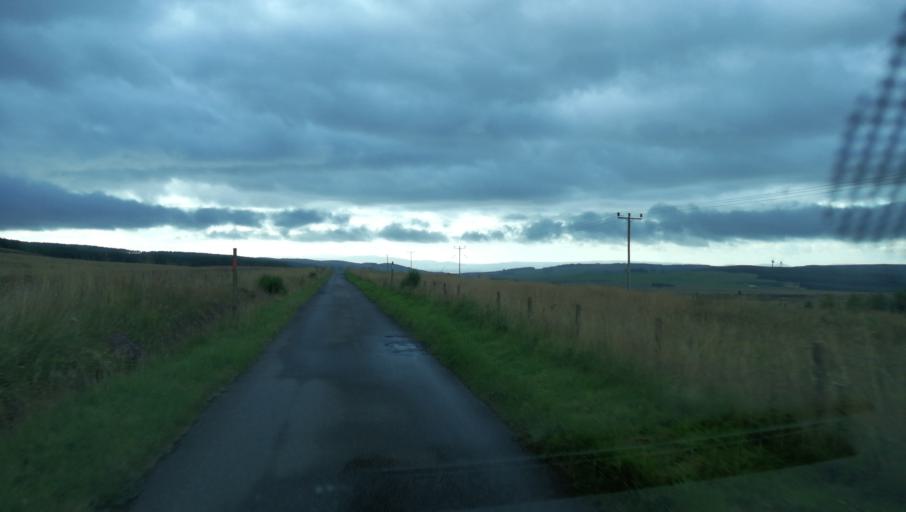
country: GB
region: Scotland
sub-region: Perth and Kinross
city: Blairgowrie
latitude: 56.6675
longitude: -3.3378
